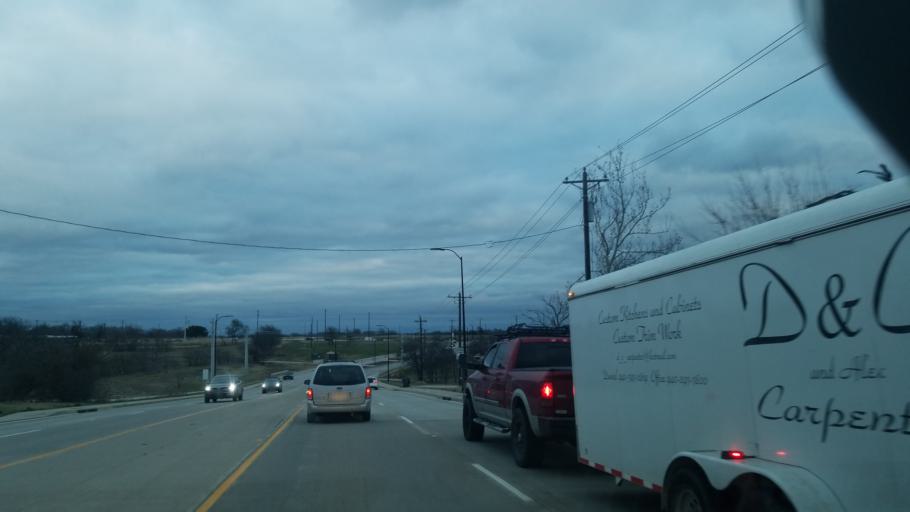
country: US
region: Texas
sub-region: Denton County
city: Little Elm
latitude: 33.1616
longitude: -96.9691
